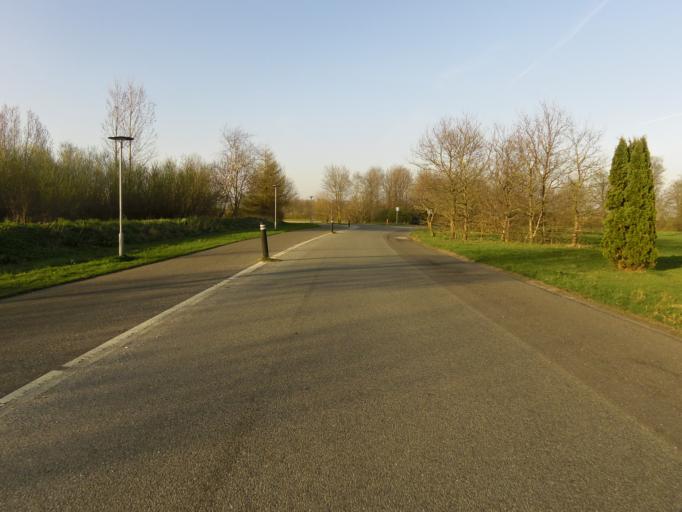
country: DK
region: South Denmark
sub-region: Vejen Kommune
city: Vejen
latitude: 55.4713
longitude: 9.1201
